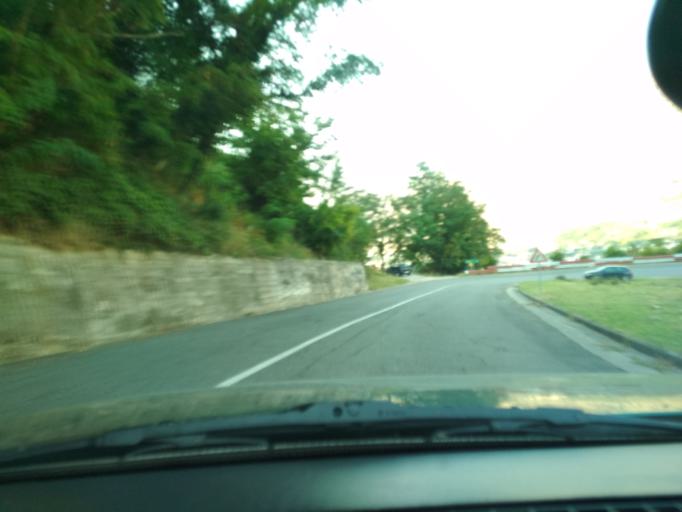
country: ME
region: Kotor
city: Kotor
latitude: 42.4216
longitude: 18.7584
